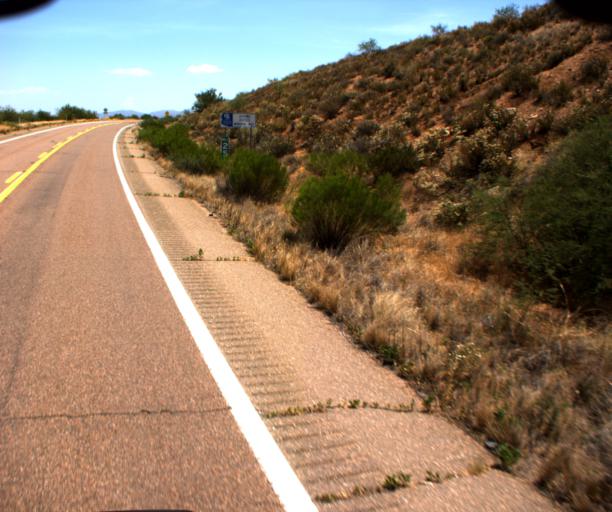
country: US
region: Arizona
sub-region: Gila County
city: Tonto Basin
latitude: 33.8008
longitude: -111.2709
